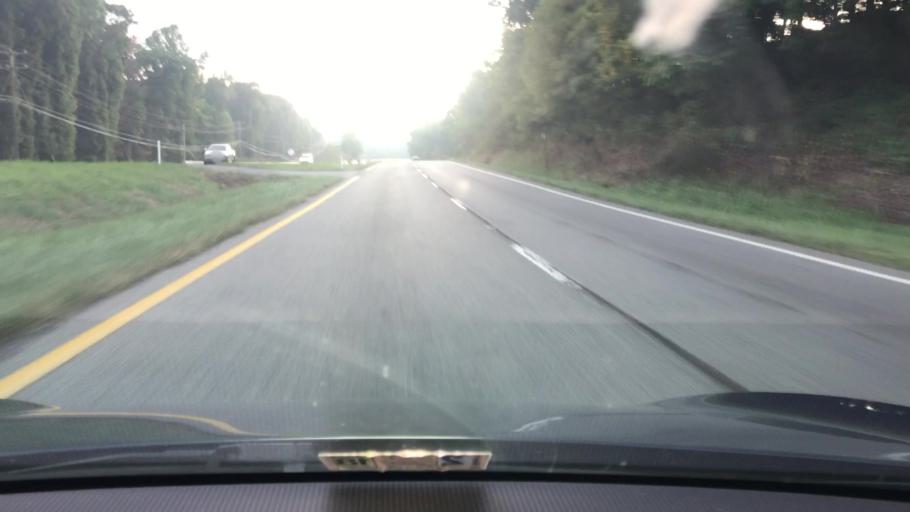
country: US
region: Virginia
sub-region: Botetourt County
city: Blue Ridge
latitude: 37.3971
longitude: -79.7614
